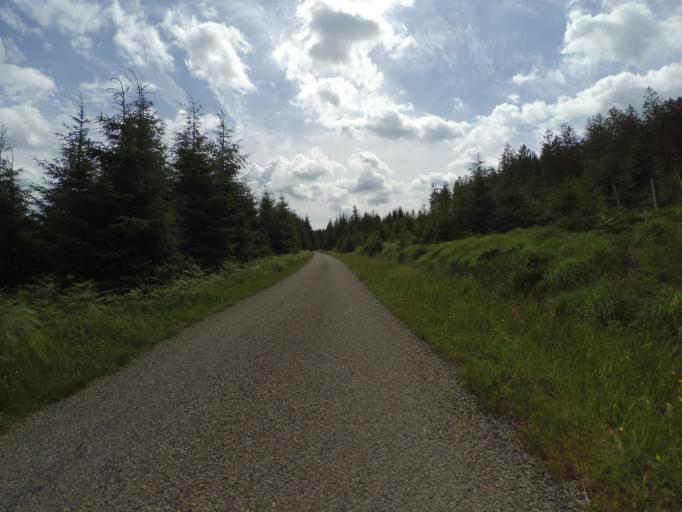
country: BE
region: Wallonia
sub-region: Province de Liege
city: Raeren
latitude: 50.5944
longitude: 6.1319
